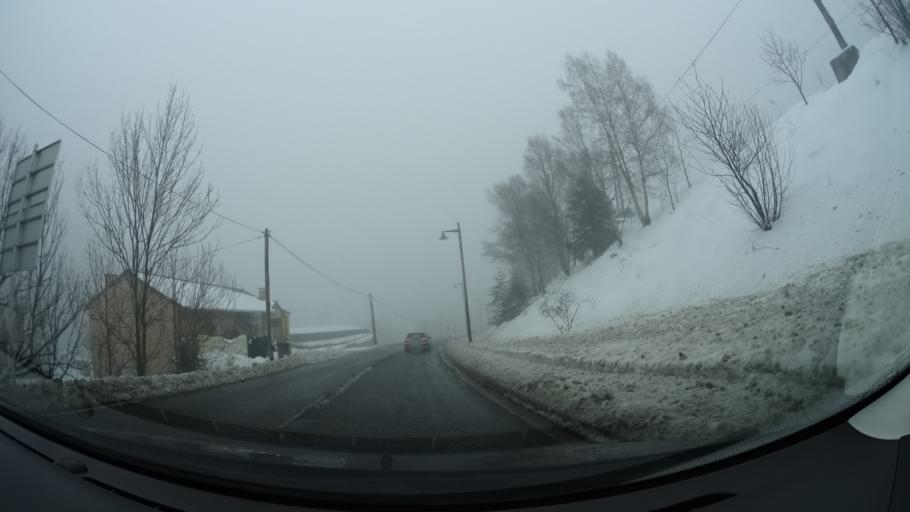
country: AD
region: Encamp
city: Pas de la Casa
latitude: 42.5898
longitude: 1.7998
